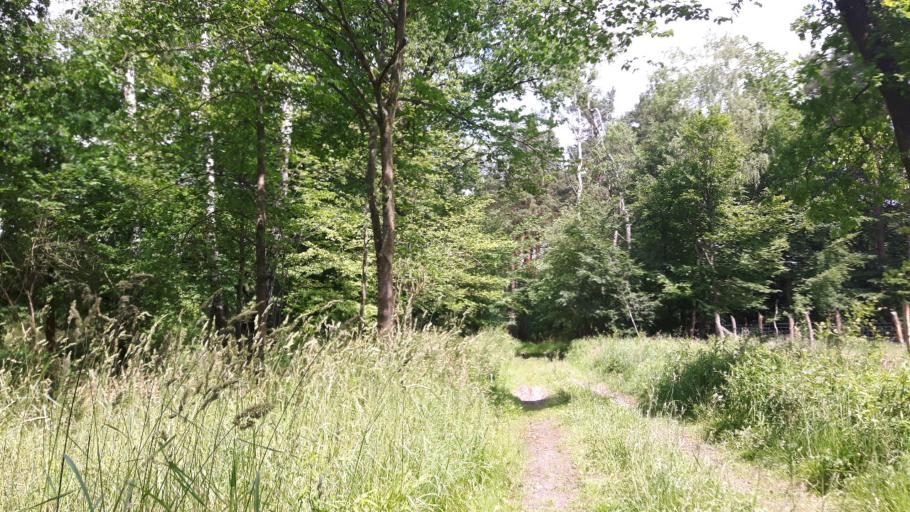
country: PL
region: West Pomeranian Voivodeship
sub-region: Powiat goleniowski
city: Goleniow
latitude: 53.6095
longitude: 14.8779
